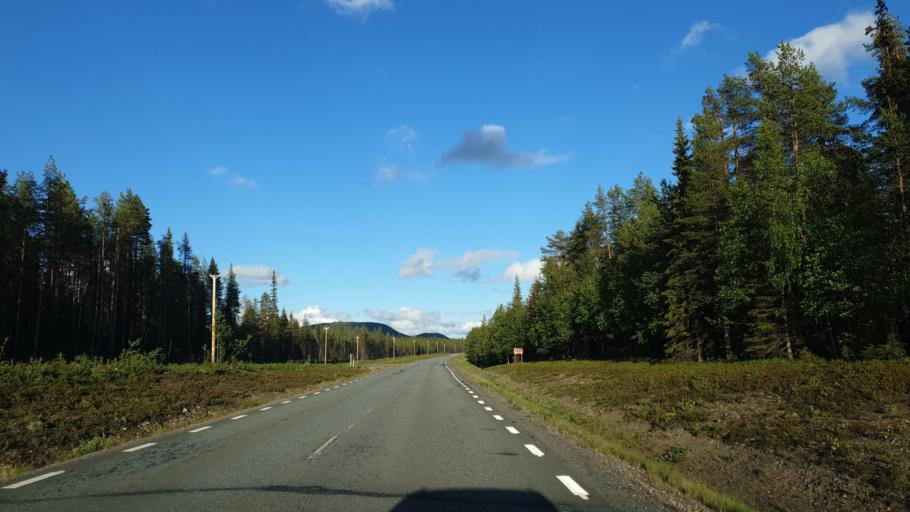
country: SE
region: Norrbotten
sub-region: Arvidsjaurs Kommun
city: Arvidsjaur
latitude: 65.7261
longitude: 18.6734
